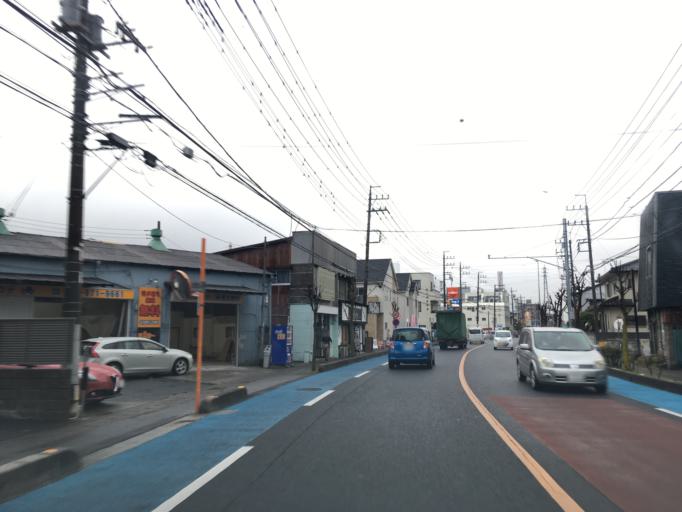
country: JP
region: Saitama
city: Koshigaya
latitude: 35.8857
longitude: 139.7919
